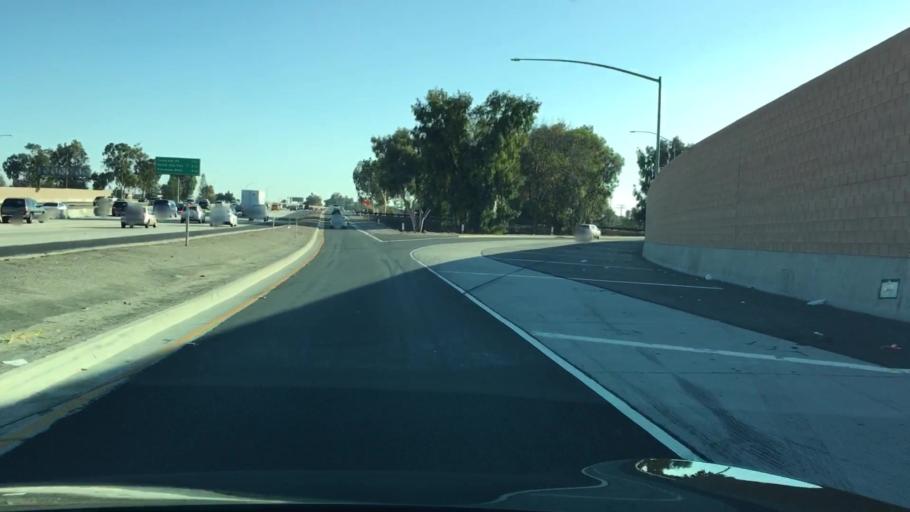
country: US
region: California
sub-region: Los Angeles County
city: West Whittier-Los Nietos
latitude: 33.9765
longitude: -118.0796
